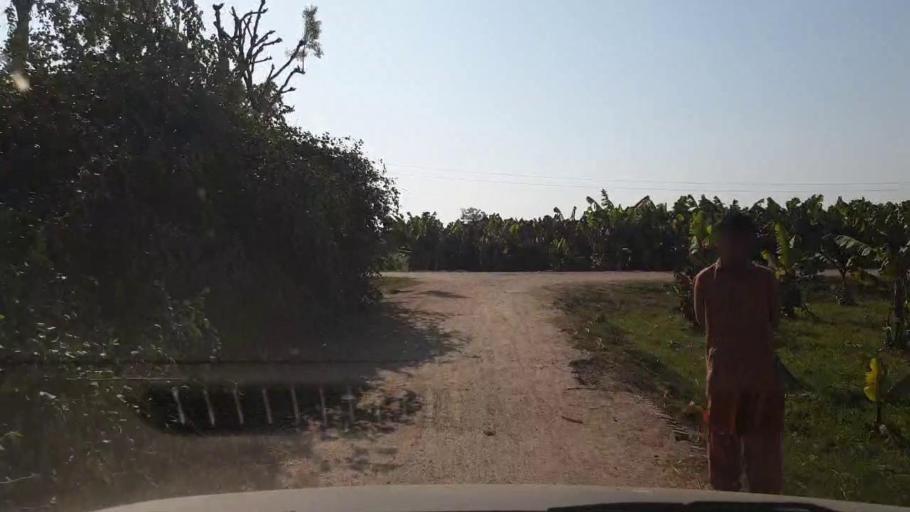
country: PK
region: Sindh
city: Tando Jam
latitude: 25.4415
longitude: 68.5981
